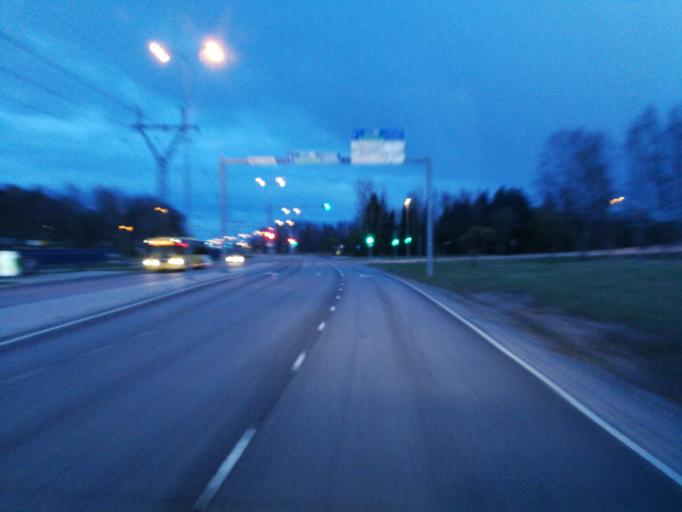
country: FI
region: Varsinais-Suomi
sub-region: Turku
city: Raisio
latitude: 60.4550
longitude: 22.1945
